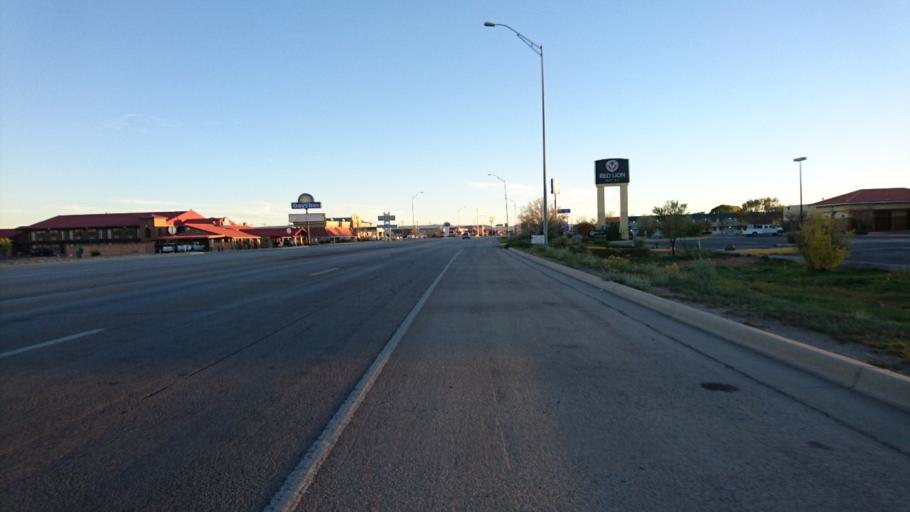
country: US
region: New Mexico
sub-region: Cibola County
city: Grants
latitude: 35.1320
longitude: -107.8275
